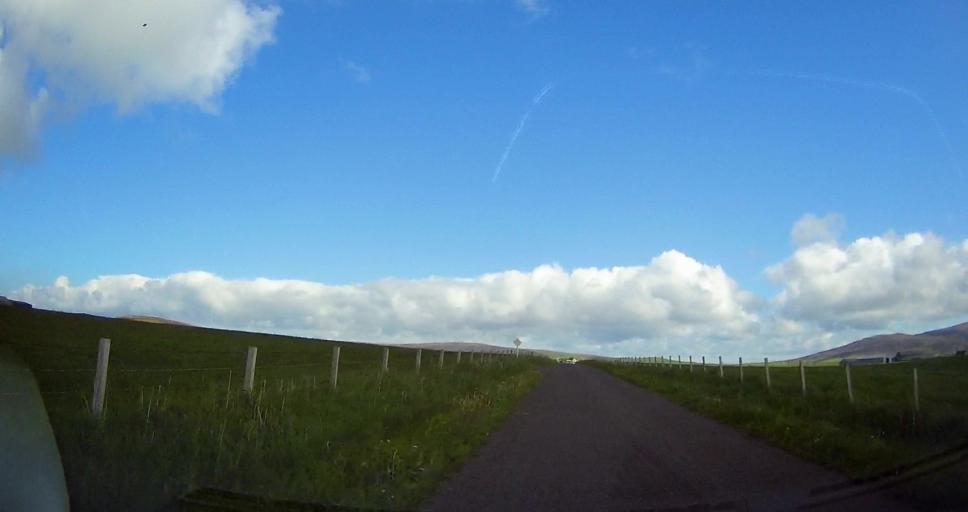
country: GB
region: Scotland
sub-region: Orkney Islands
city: Stromness
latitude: 59.0000
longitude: -3.1718
